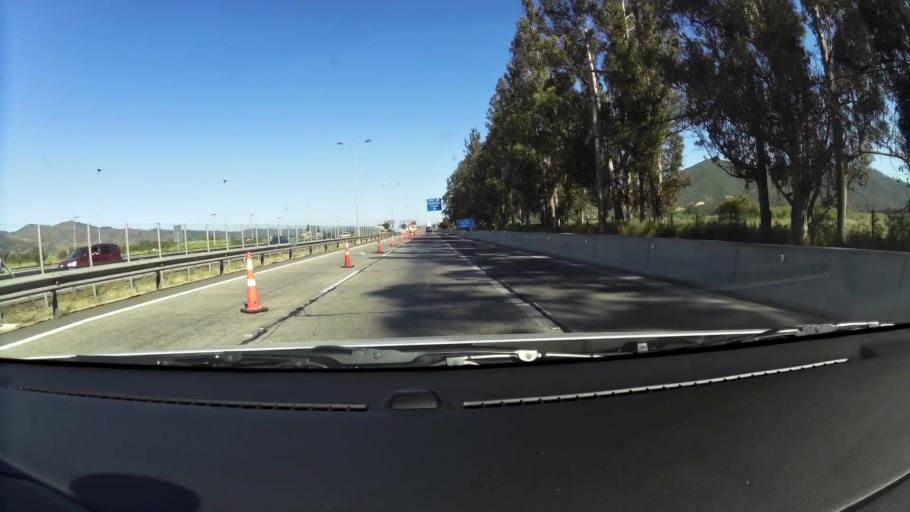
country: CL
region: Valparaiso
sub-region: Provincia de Marga Marga
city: Villa Alemana
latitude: -33.3403
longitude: -71.3669
